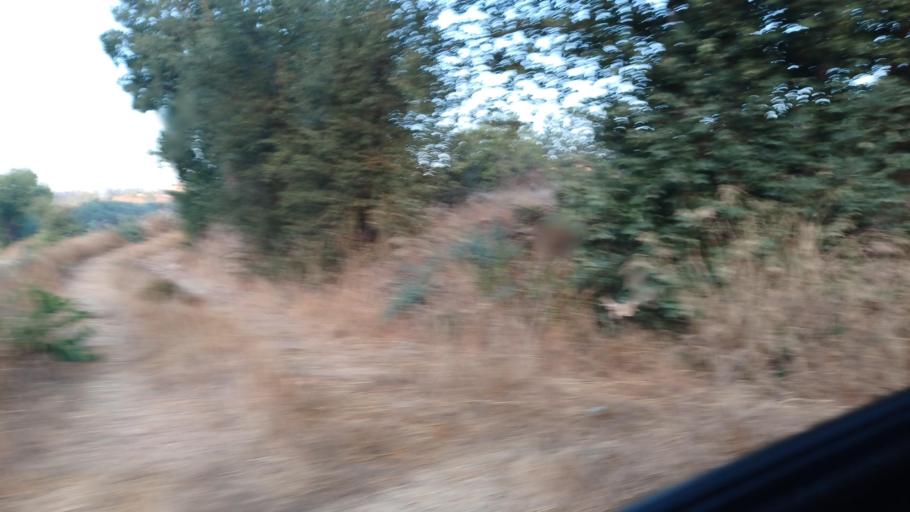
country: CY
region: Pafos
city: Mesogi
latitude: 34.8563
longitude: 32.5581
